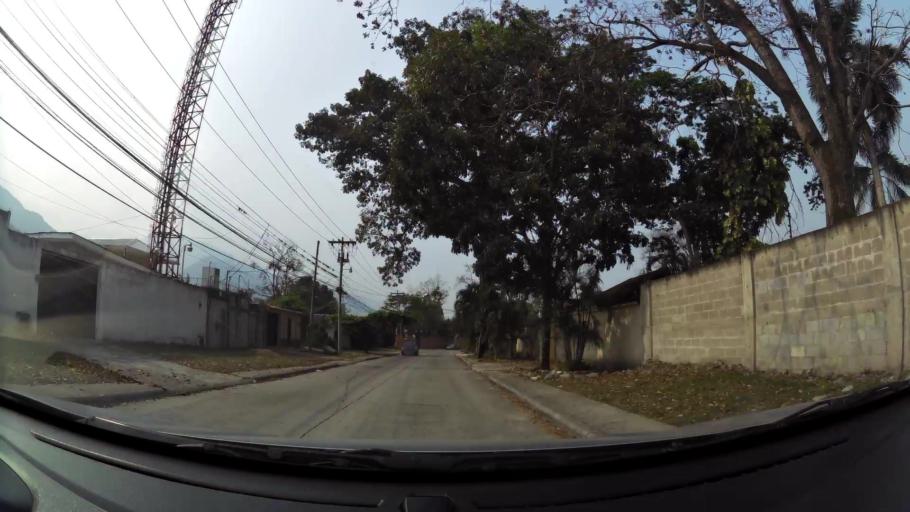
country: HN
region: Cortes
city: El Zapotal del Norte
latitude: 15.5097
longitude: -88.0438
